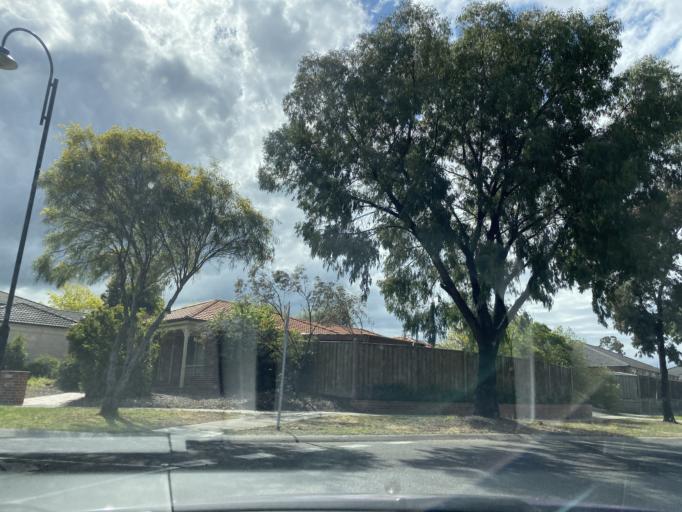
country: AU
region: Victoria
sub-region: Whittlesea
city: Mernda
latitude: -37.6245
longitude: 145.0923
